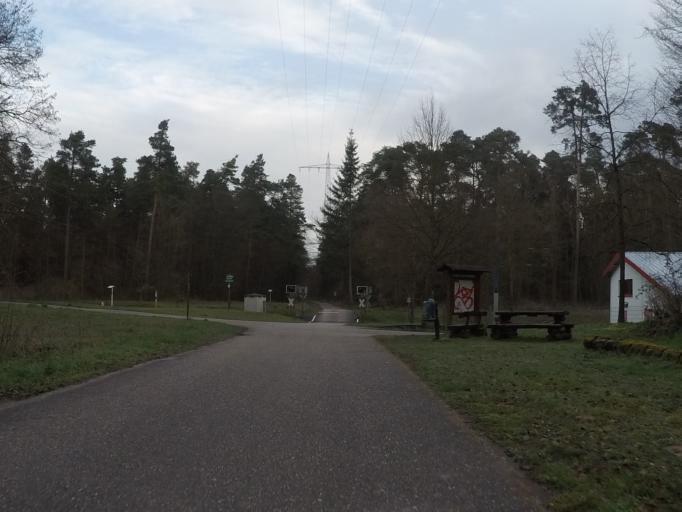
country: DE
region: Rheinland-Pfalz
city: Worth am Rhein
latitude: 49.0596
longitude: 8.2404
